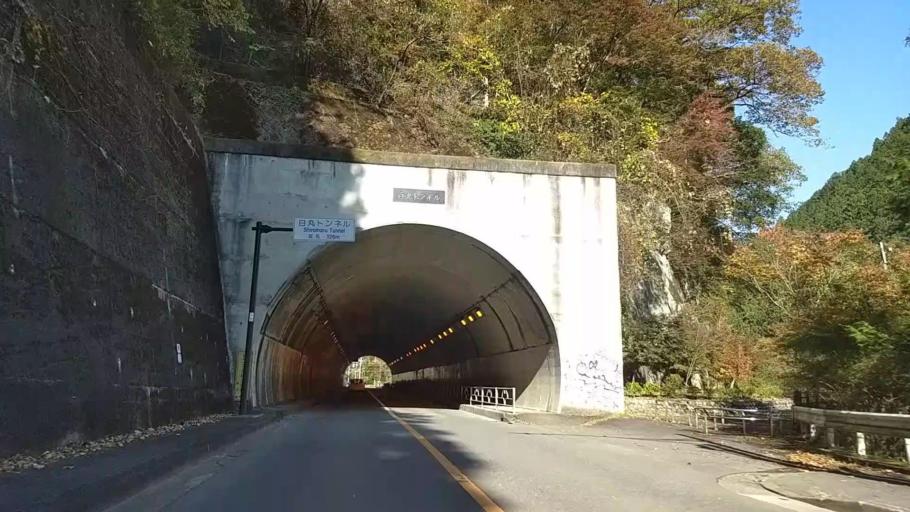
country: JP
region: Tokyo
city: Ome
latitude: 35.8080
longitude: 139.1130
